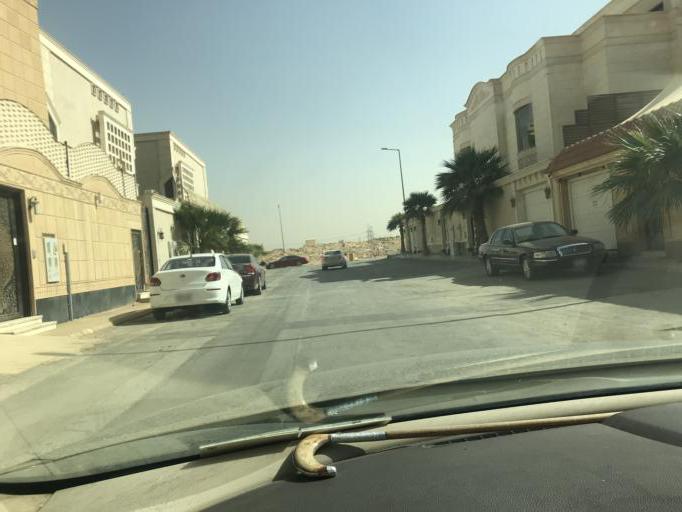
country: SA
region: Ar Riyad
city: Riyadh
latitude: 24.8265
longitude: 46.7310
